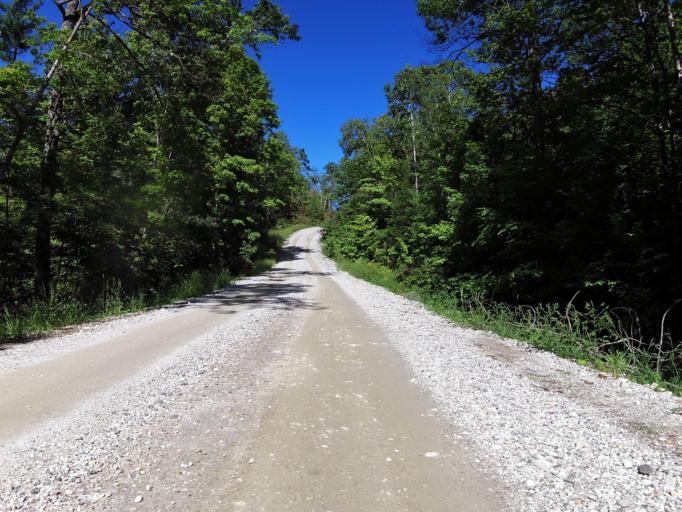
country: CA
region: Ontario
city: Renfrew
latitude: 45.1320
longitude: -76.7130
